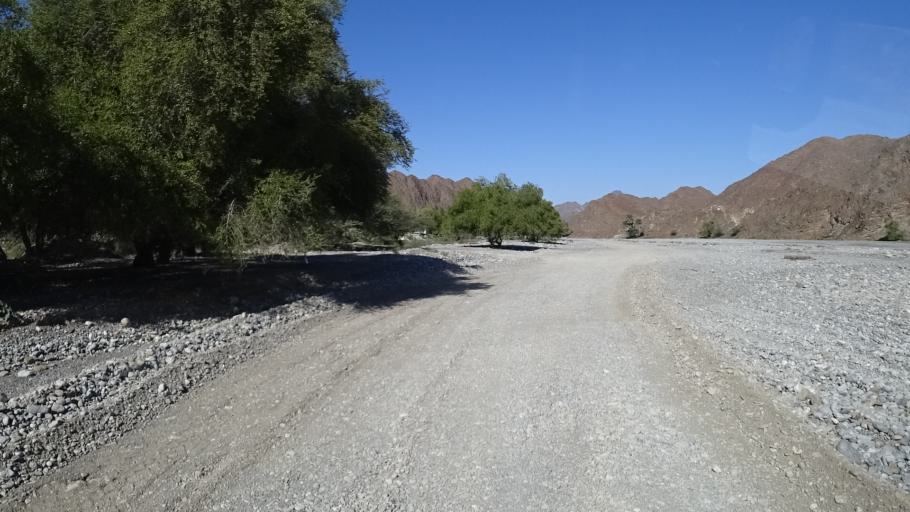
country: OM
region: Al Batinah
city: Bayt al `Awabi
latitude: 23.3925
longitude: 57.6624
